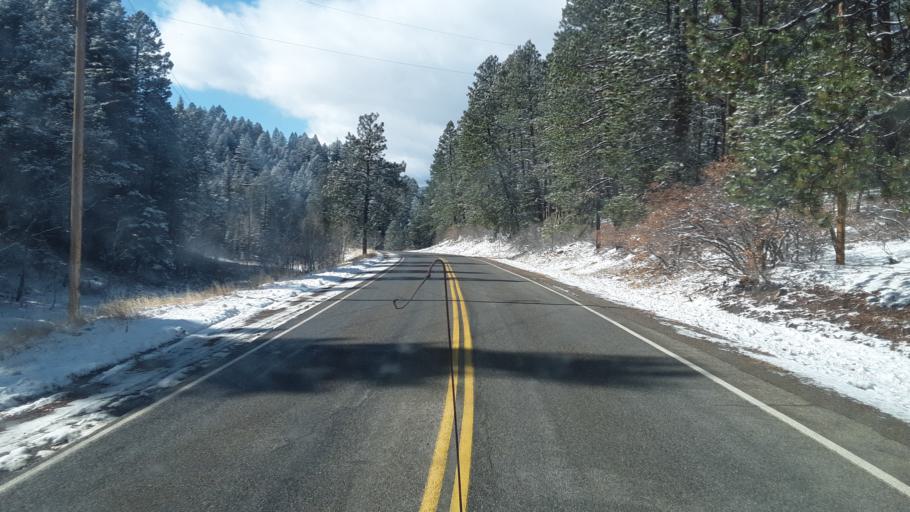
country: US
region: Colorado
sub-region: La Plata County
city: Bayfield
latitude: 37.3580
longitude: -107.6643
